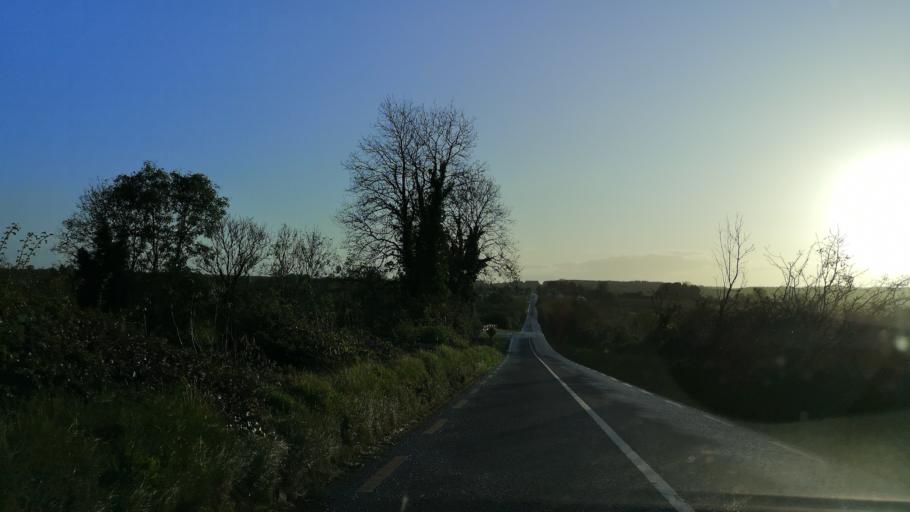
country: IE
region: Connaught
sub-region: Roscommon
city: Castlerea
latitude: 53.7501
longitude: -8.5305
